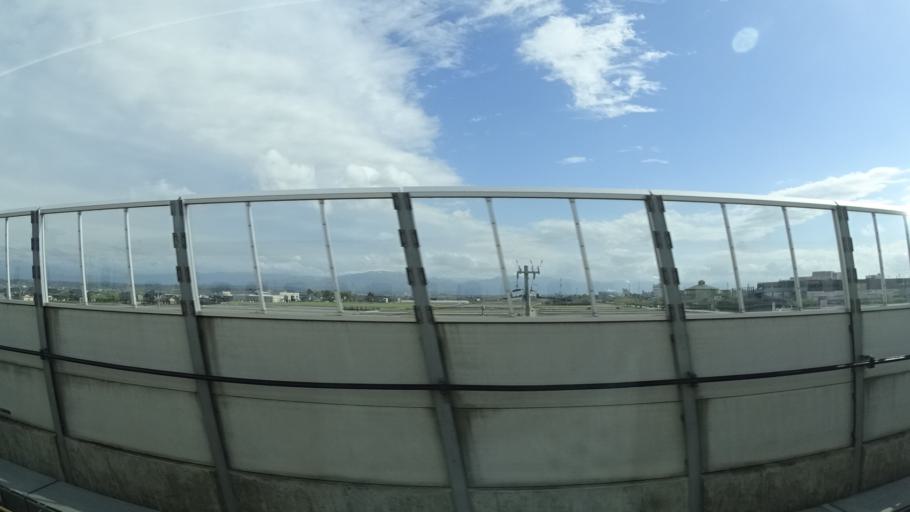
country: JP
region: Toyama
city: Takaoka
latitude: 36.7263
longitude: 137.0193
